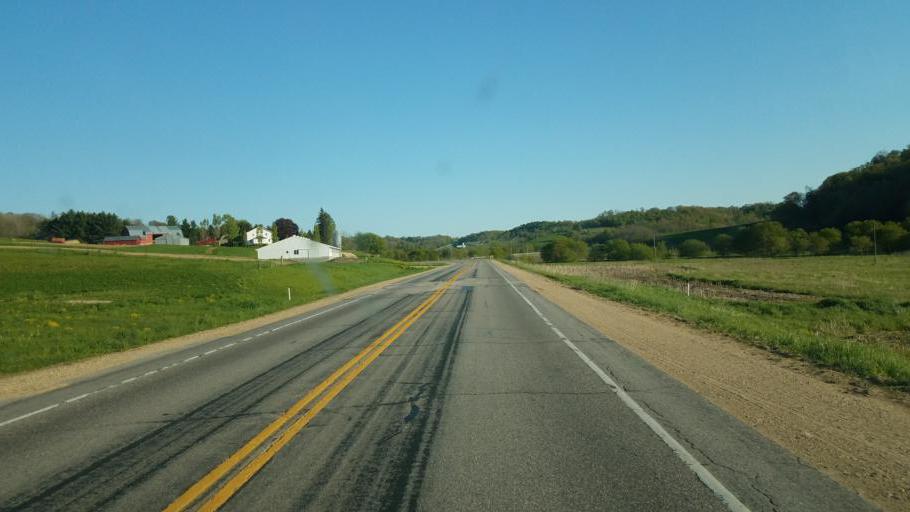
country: US
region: Wisconsin
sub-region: Vernon County
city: Hillsboro
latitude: 43.6209
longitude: -90.3583
